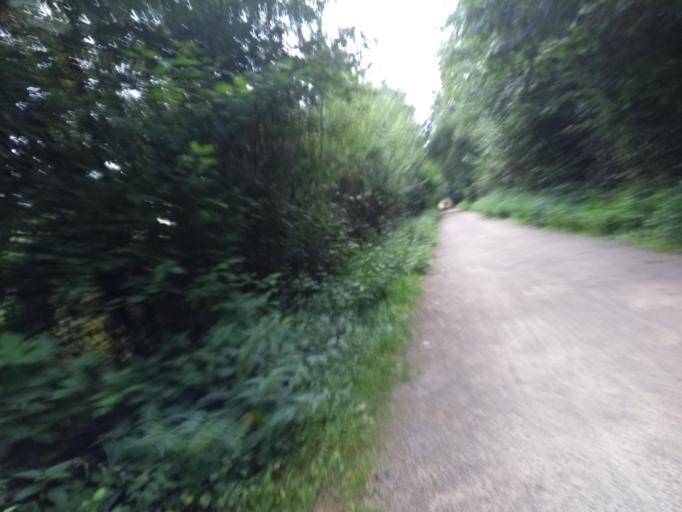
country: DE
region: North Rhine-Westphalia
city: Witten
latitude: 51.4114
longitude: 7.3439
